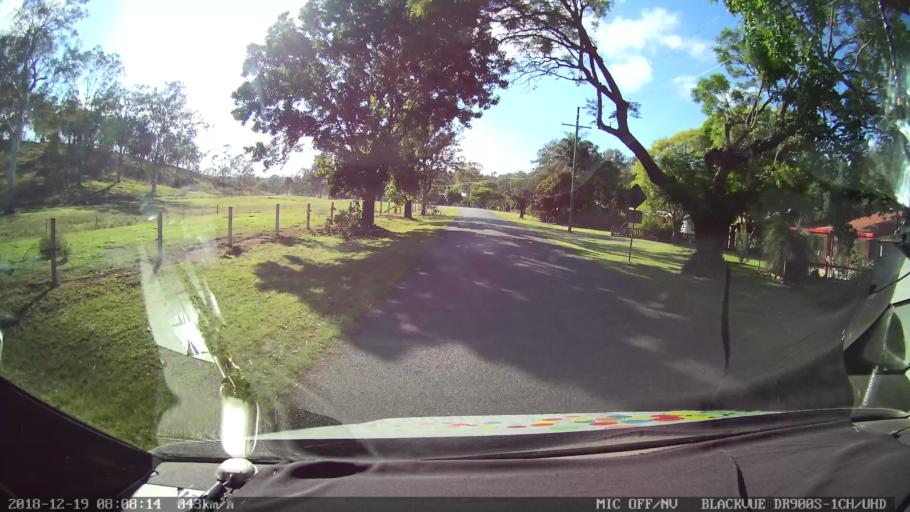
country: AU
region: Queensland
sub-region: Logan
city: Cedar Vale
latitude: -28.2117
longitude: 152.8689
